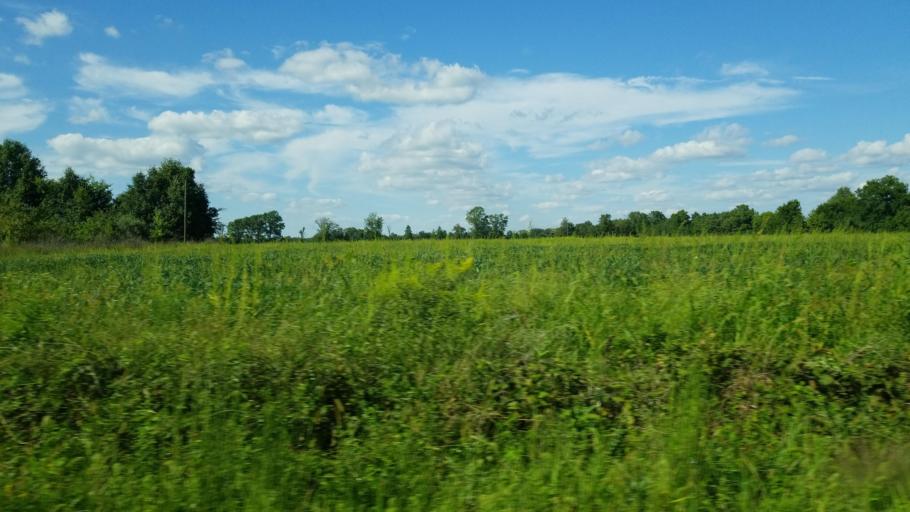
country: US
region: Illinois
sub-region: Saline County
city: Harrisburg
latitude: 37.8127
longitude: -88.5552
